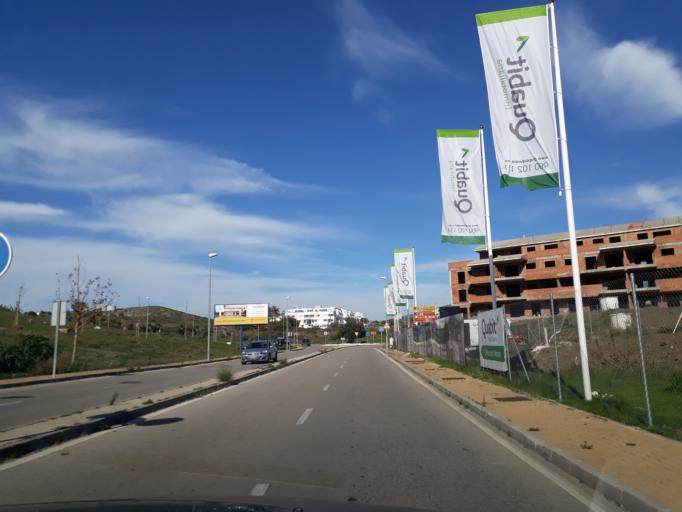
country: ES
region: Andalusia
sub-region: Provincia de Malaga
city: Fuengirola
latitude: 36.5239
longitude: -4.6866
